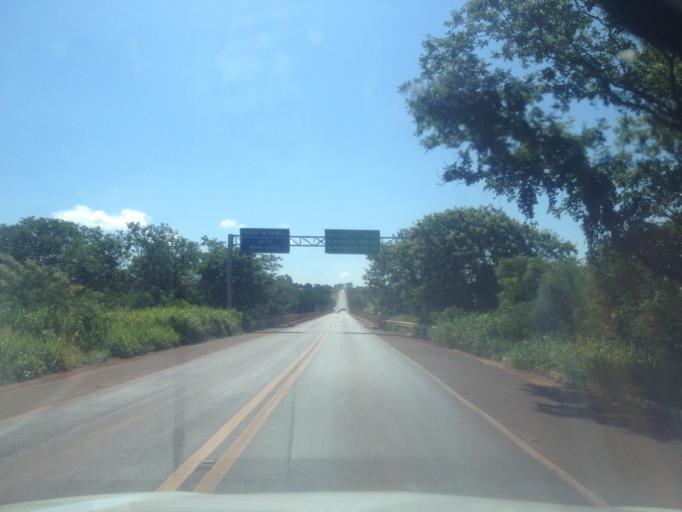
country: BR
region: Minas Gerais
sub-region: Santa Vitoria
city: Santa Vitoria
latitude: -19.0432
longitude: -50.5042
